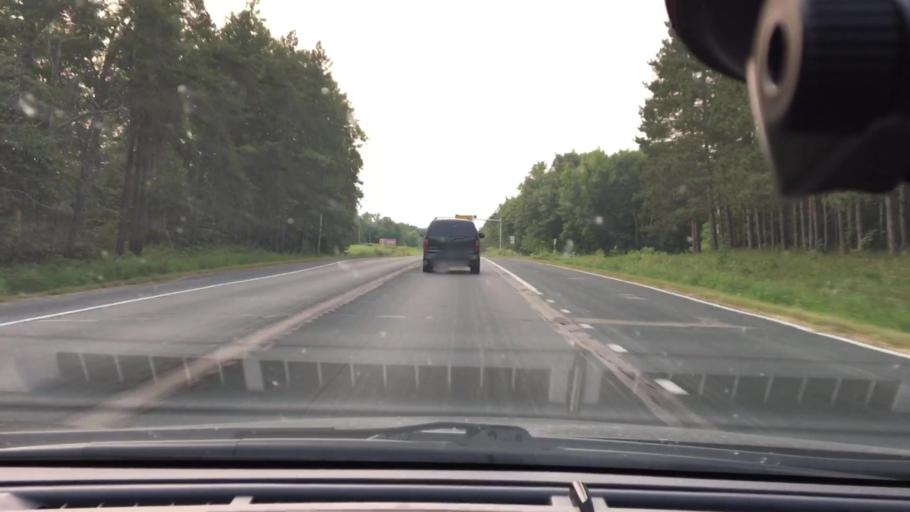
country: US
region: Minnesota
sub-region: Mille Lacs County
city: Vineland
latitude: 46.2465
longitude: -93.8116
